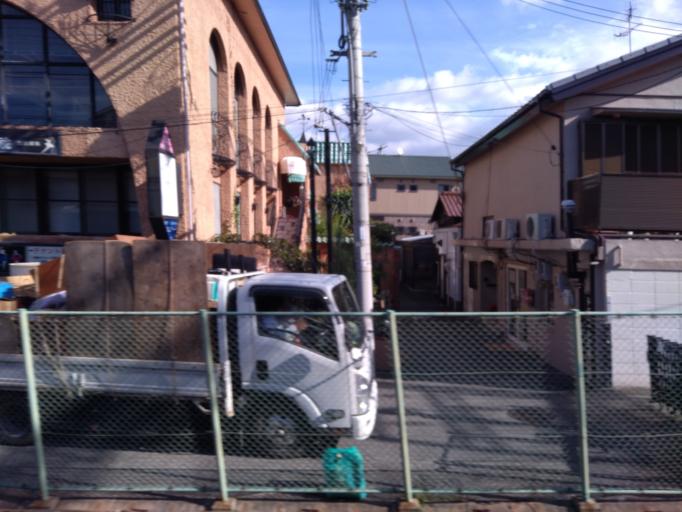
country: JP
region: Osaka
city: Ikeda
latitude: 34.8058
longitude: 135.4458
